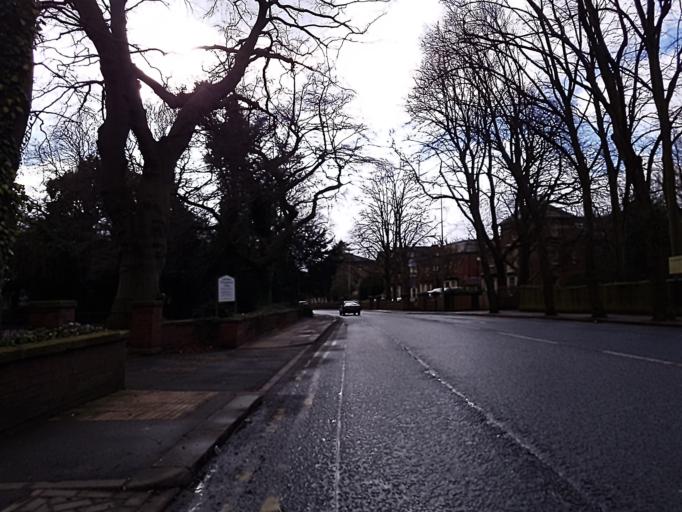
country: GB
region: England
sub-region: North East Lincolnshire
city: Grimbsy
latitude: 53.5615
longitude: -0.0921
